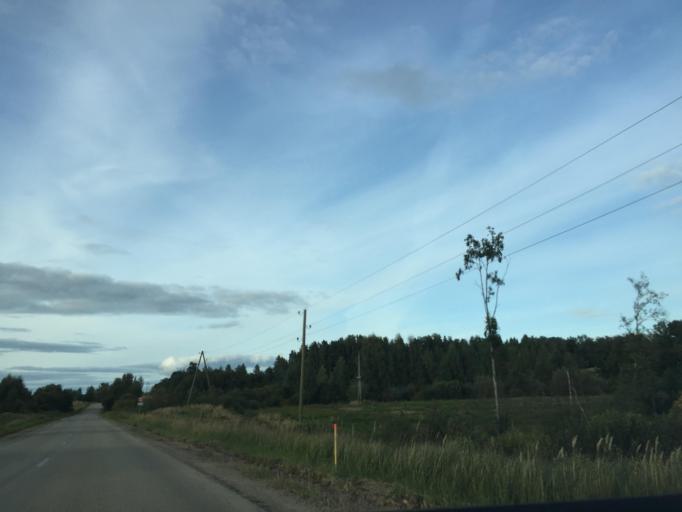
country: LV
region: Viesite
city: Viesite
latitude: 56.3091
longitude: 25.4465
